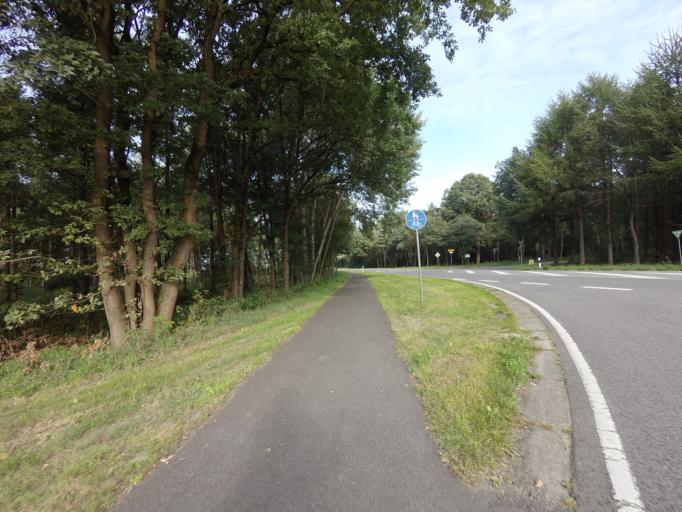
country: DE
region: Lower Saxony
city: Itterbeck
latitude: 52.5129
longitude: 6.7753
